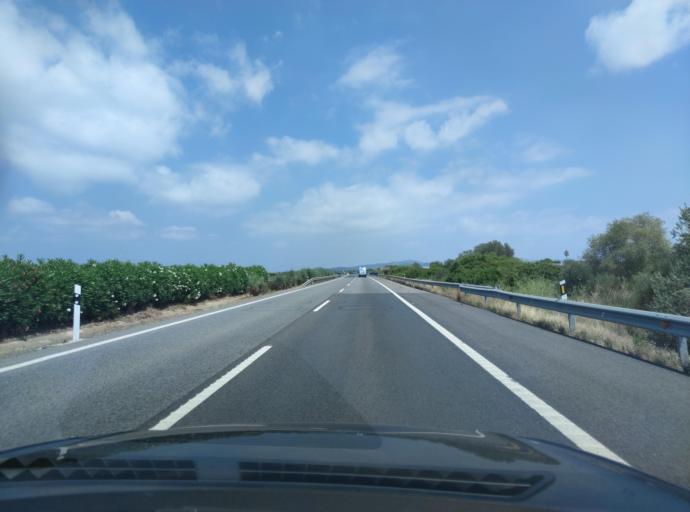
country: ES
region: Catalonia
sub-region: Provincia de Tarragona
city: Alcanar
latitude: 40.5341
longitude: 0.4188
